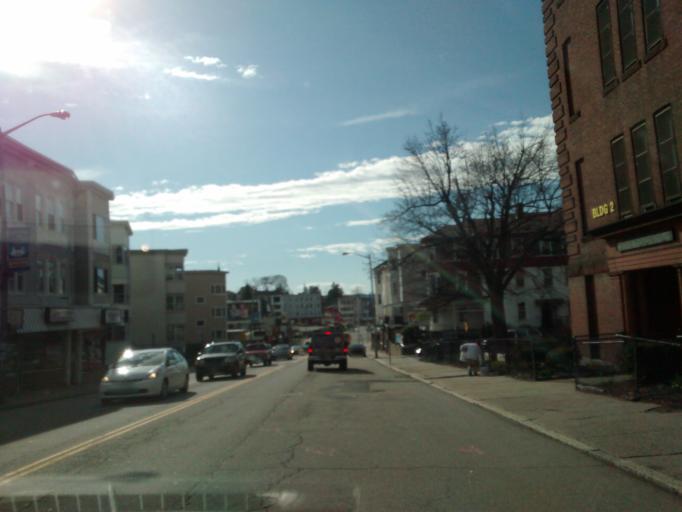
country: US
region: Massachusetts
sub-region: Worcester County
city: Worcester
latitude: 42.2561
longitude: -71.7872
